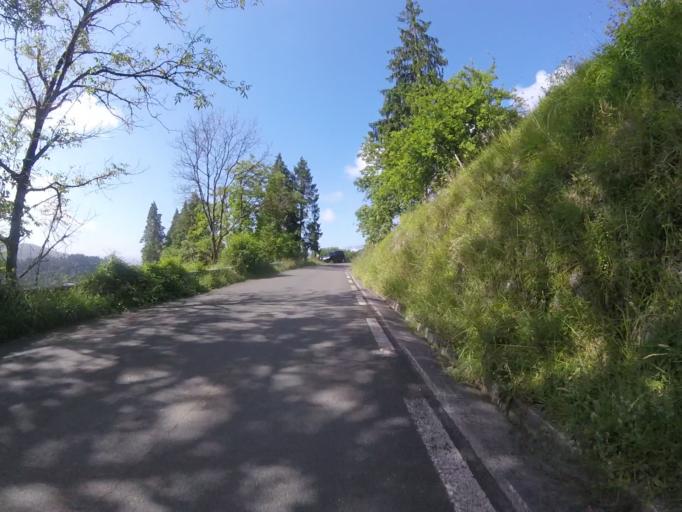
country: ES
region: Basque Country
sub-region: Provincia de Guipuzcoa
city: Ormaiztegui
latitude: 43.0840
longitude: -2.2384
